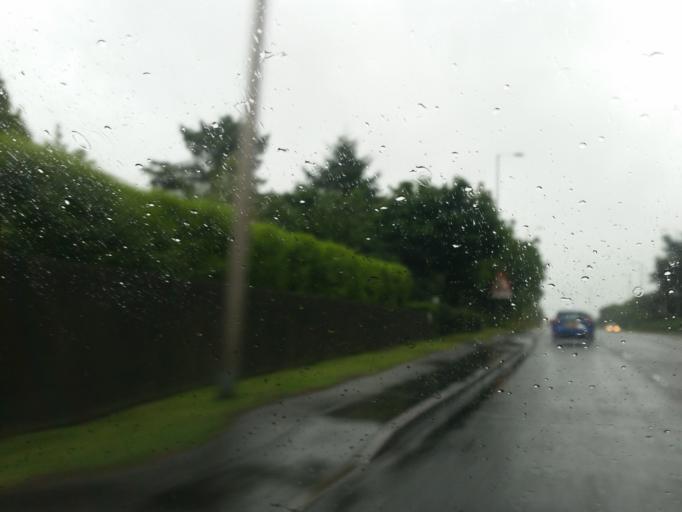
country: GB
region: Northern Ireland
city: Holywood
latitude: 54.6570
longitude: -5.7684
